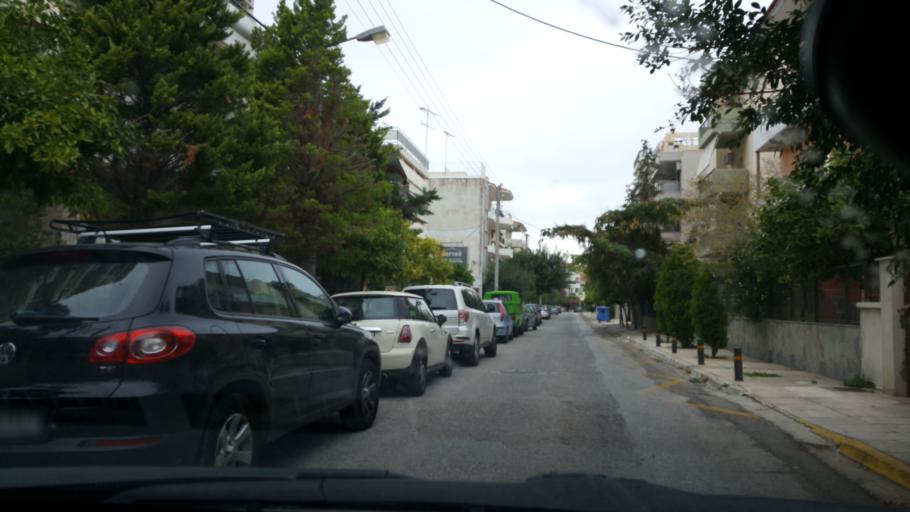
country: GR
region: Attica
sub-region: Nomarchia Athinas
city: Argyroupoli
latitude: 37.8937
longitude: 23.7500
